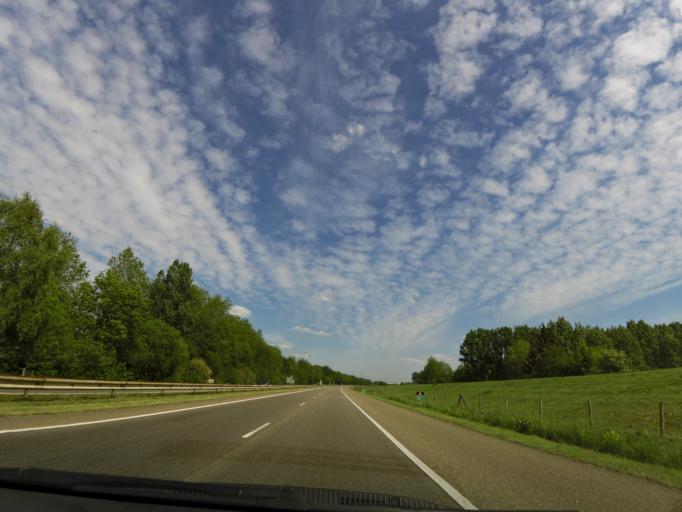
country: NL
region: Limburg
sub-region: Gemeente Leudal
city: Haelen
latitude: 51.2040
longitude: 5.9377
